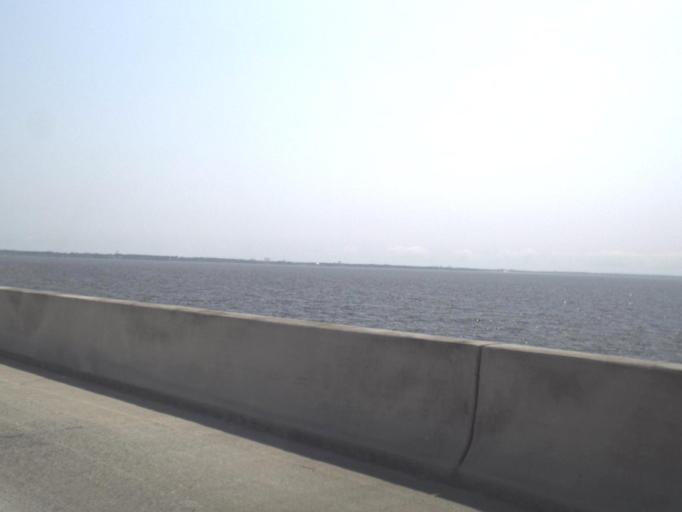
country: US
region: Florida
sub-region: Santa Rosa County
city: Oriole Beach
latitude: 30.4379
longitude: -87.0997
